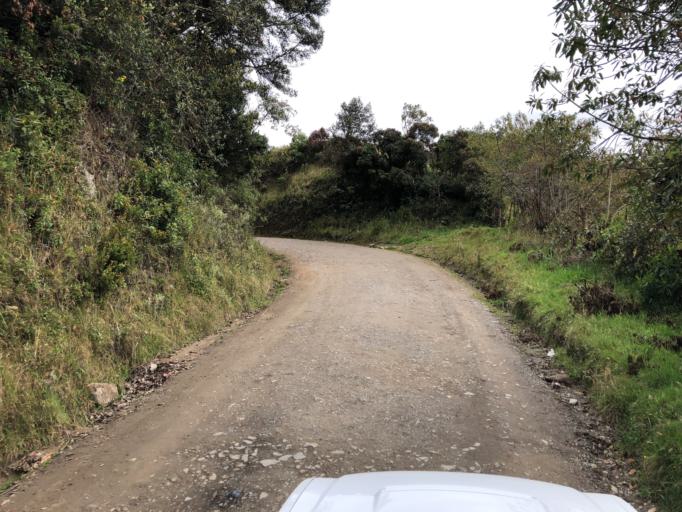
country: CO
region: Cauca
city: Totoro
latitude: 2.5003
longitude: -76.3573
